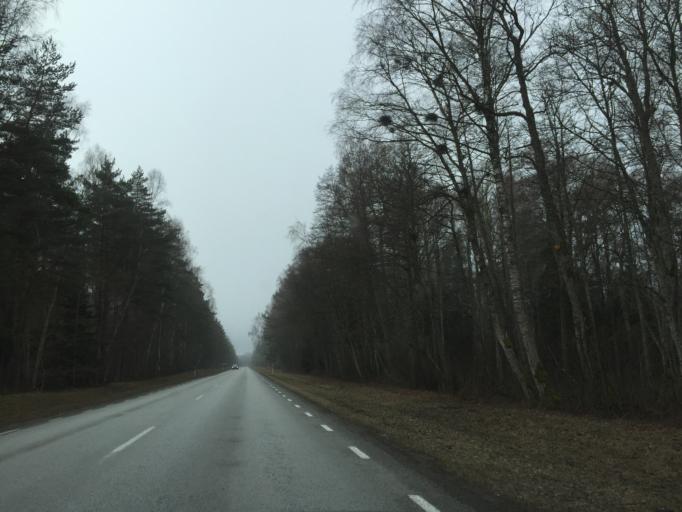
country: EE
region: Saare
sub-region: Kuressaare linn
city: Kuressaare
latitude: 58.1899
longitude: 22.2660
